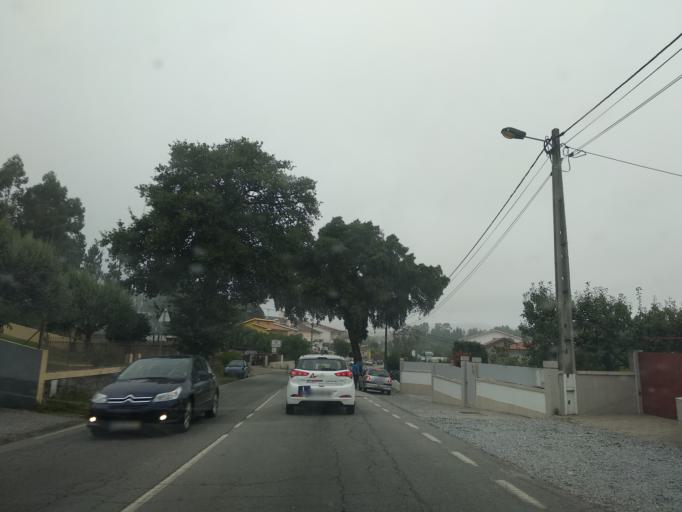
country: PT
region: Braga
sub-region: Vila Verde
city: Vila Verde
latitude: 41.6359
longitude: -8.4334
